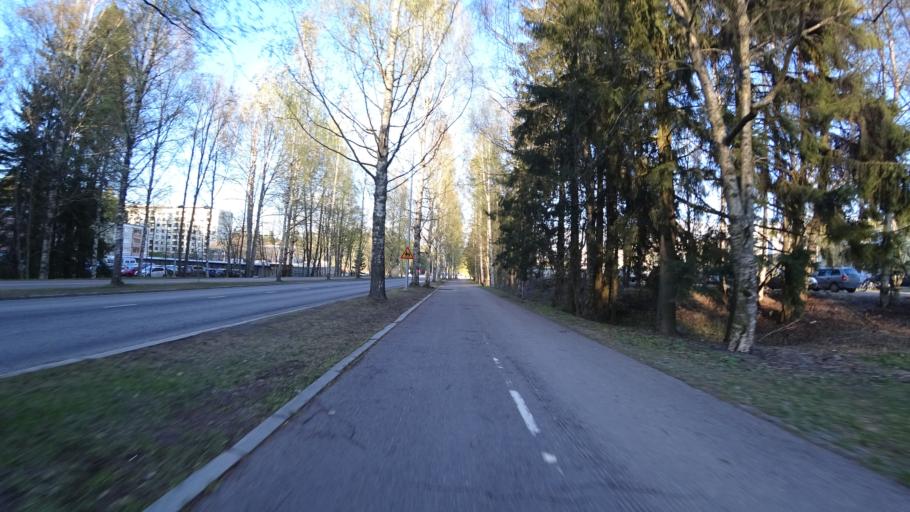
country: FI
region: Pirkanmaa
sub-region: Tampere
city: Pirkkala
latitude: 61.5045
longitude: 23.6142
